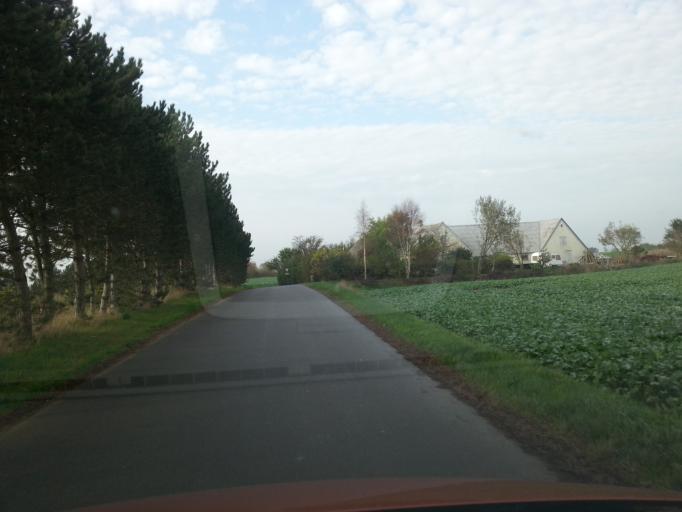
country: DK
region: Zealand
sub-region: Guldborgsund Kommune
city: Stubbekobing
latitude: 54.9289
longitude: 12.0185
